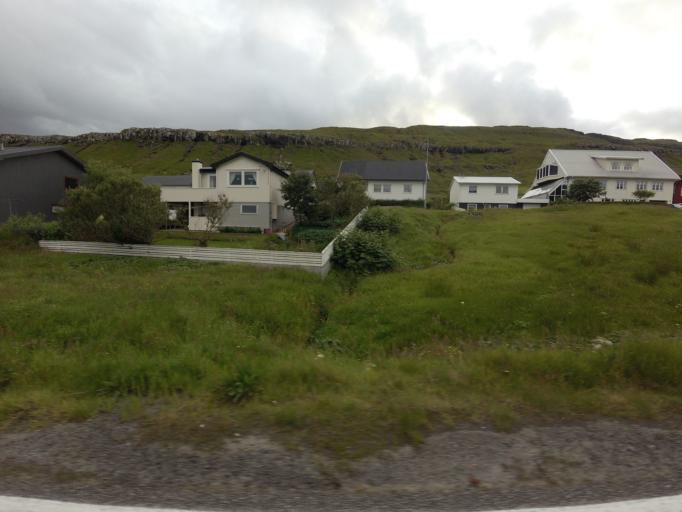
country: FO
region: Streymoy
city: Kollafjordhur
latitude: 62.1255
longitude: -6.8753
